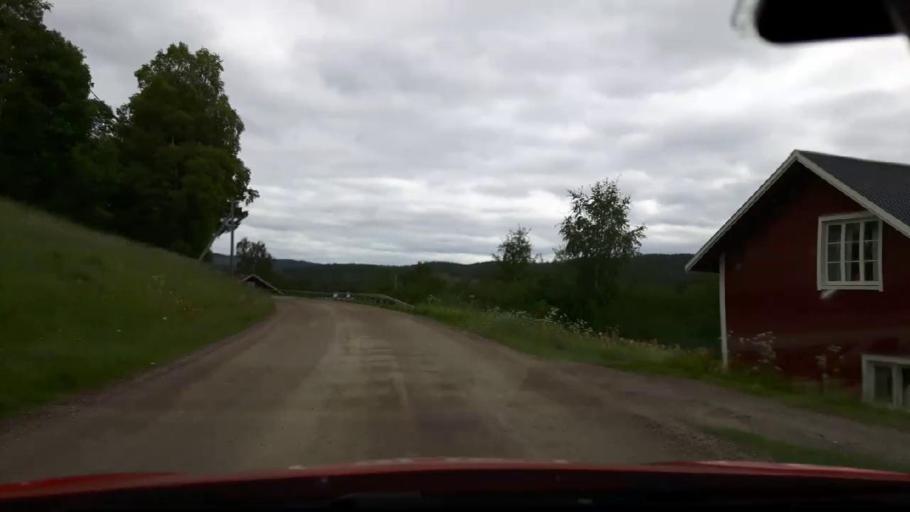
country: SE
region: Jaemtland
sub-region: Ragunda Kommun
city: Hammarstrand
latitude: 63.1623
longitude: 16.2188
